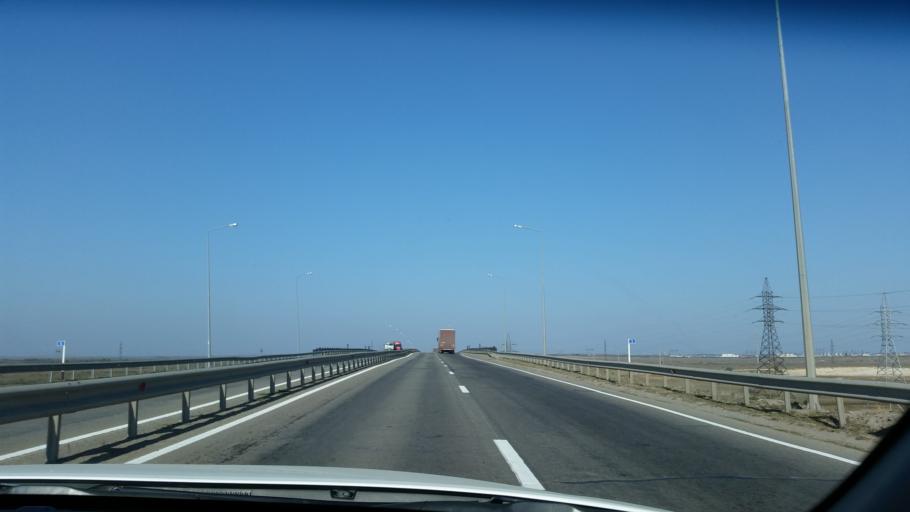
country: KZ
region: Astana Qalasy
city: Astana
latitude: 51.2267
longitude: 71.3251
